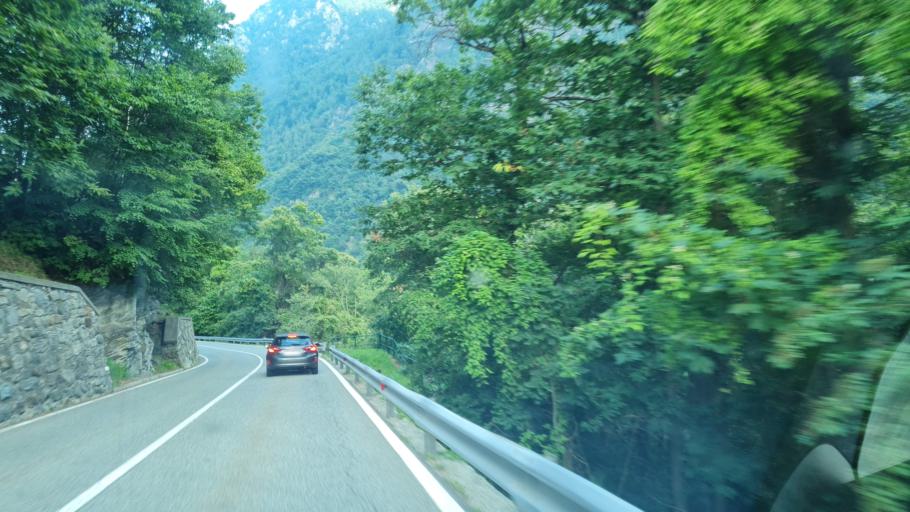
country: IT
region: Aosta Valley
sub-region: Valle d'Aosta
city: Pont-Bozet
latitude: 45.6055
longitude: 7.6910
